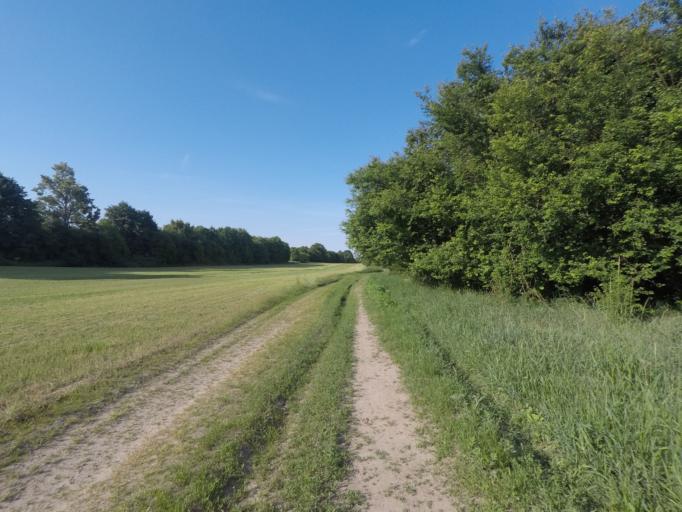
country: DE
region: Brandenburg
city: Marienwerder
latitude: 52.8688
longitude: 13.6865
